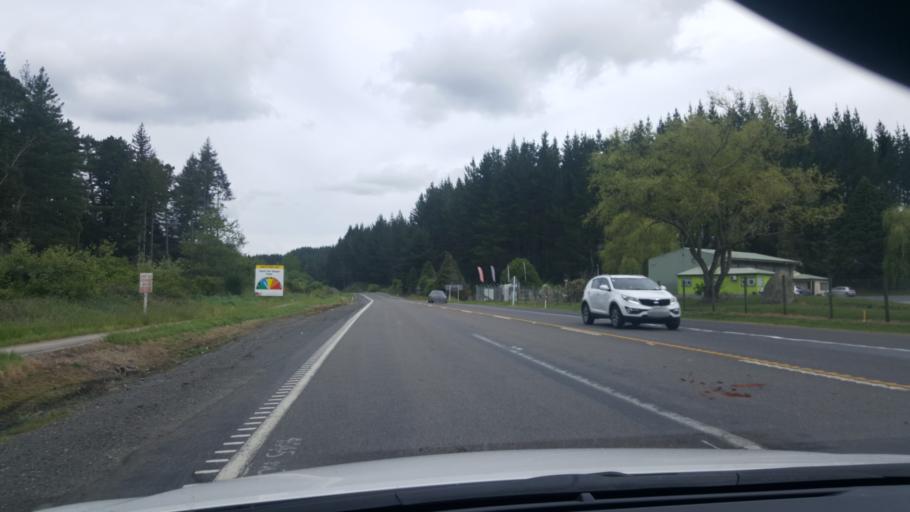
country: NZ
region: Bay of Plenty
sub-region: Rotorua District
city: Rotorua
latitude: -38.1788
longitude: 176.2493
